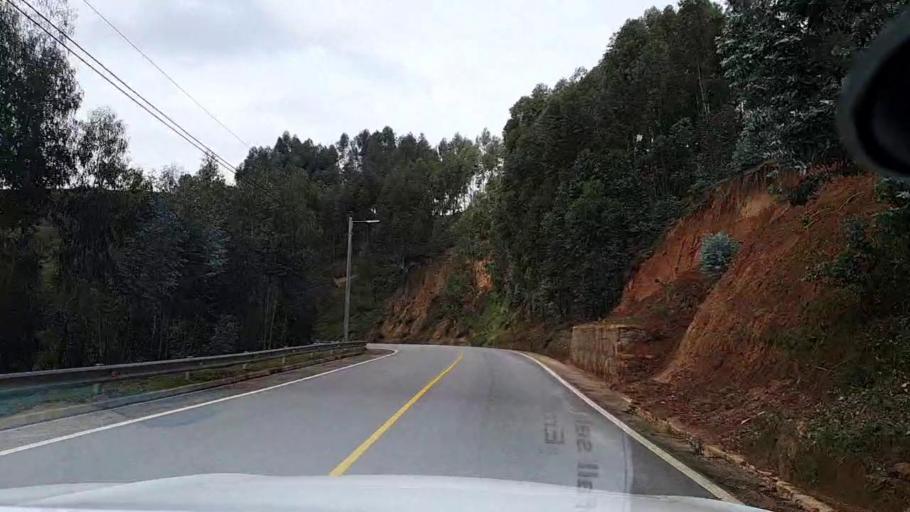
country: RW
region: Southern Province
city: Nzega
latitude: -2.5180
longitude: 29.4595
